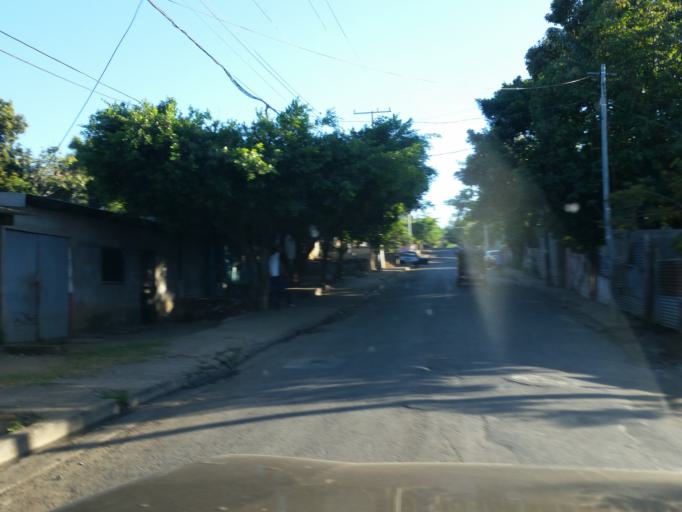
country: NI
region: Managua
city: Managua
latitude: 12.1148
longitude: -86.2898
